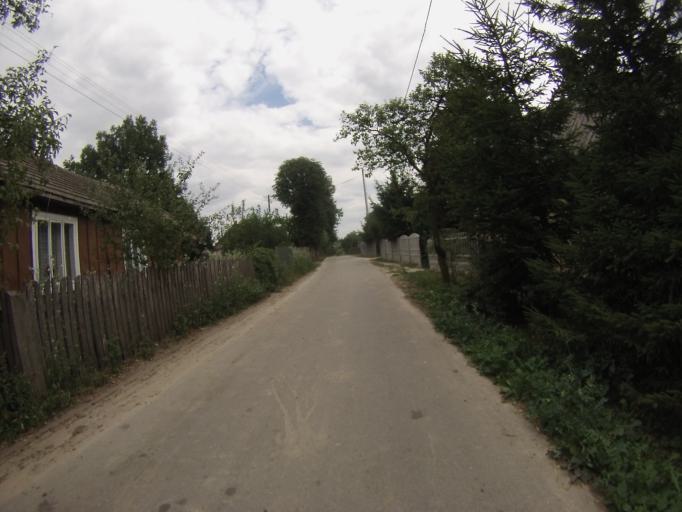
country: PL
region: Swietokrzyskie
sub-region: Powiat staszowski
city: Bogoria
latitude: 50.6861
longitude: 21.2069
